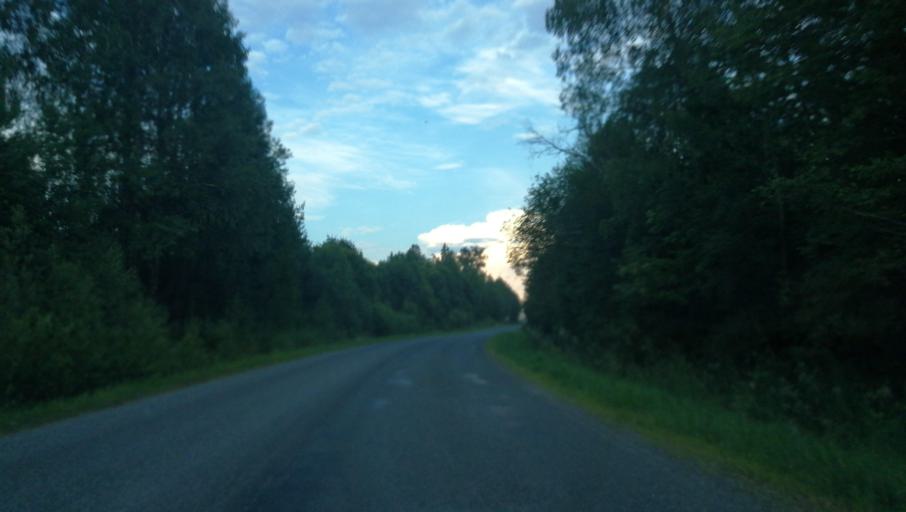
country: LV
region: Priekuli
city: Priekuli
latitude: 57.2736
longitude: 25.3327
